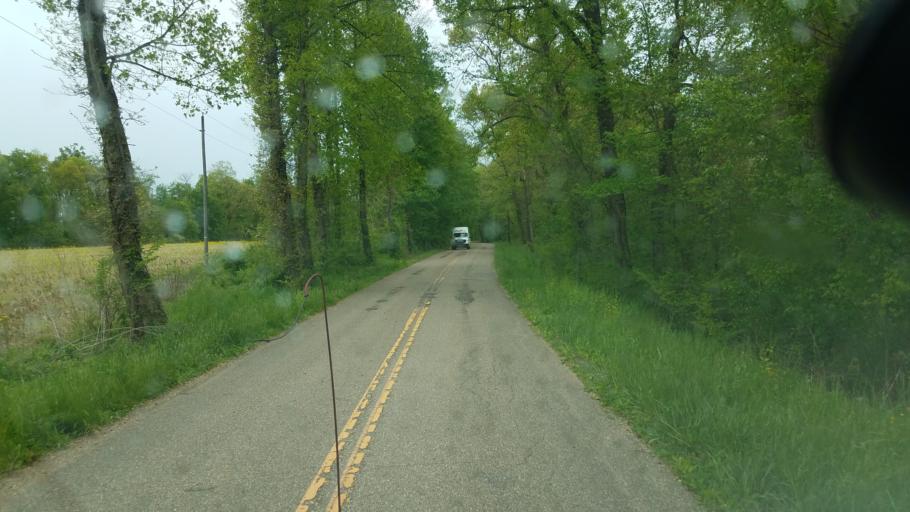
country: US
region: Ohio
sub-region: Guernsey County
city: Cambridge
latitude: 40.1427
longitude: -81.5356
